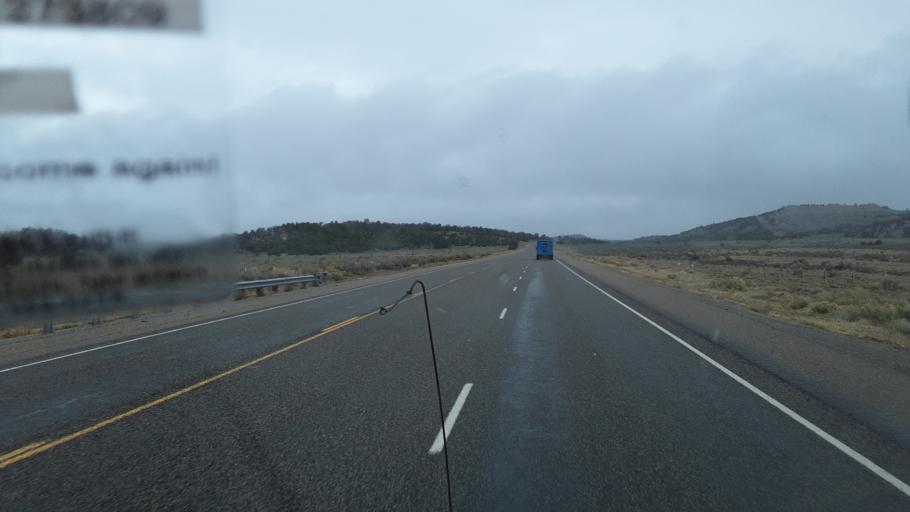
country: US
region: New Mexico
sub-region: Rio Arriba County
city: Tierra Amarilla
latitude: 36.4448
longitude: -106.4750
